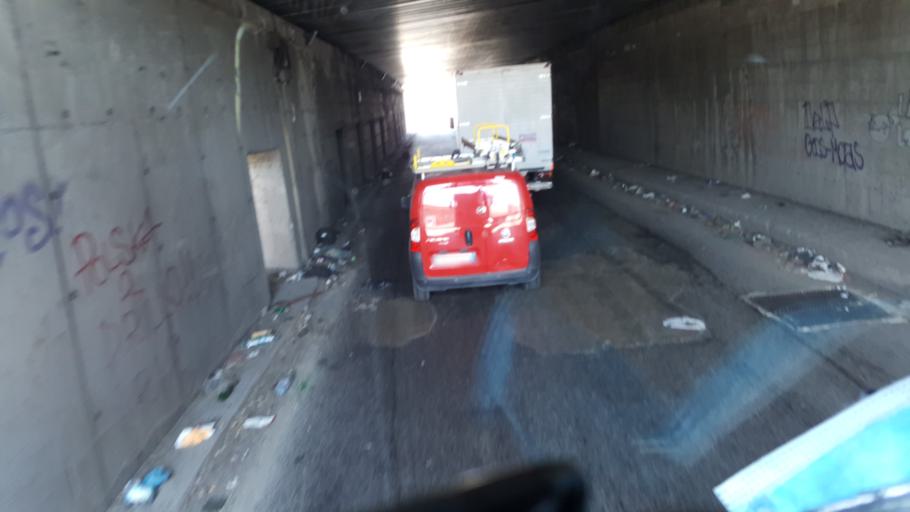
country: IT
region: Campania
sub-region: Provincia di Napoli
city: San Giorgio a Cremano
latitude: 40.8456
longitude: 14.2951
